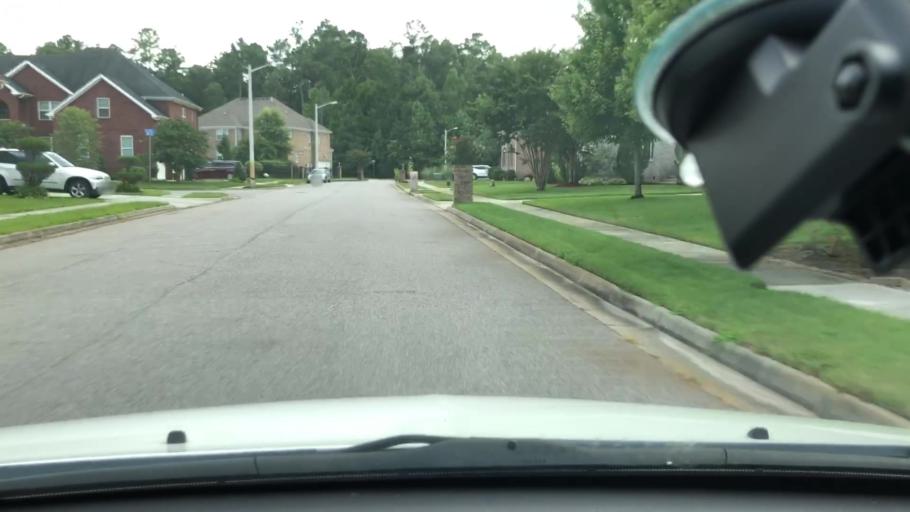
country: US
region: Virginia
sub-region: City of Chesapeake
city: Chesapeake
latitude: 36.7086
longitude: -76.2926
